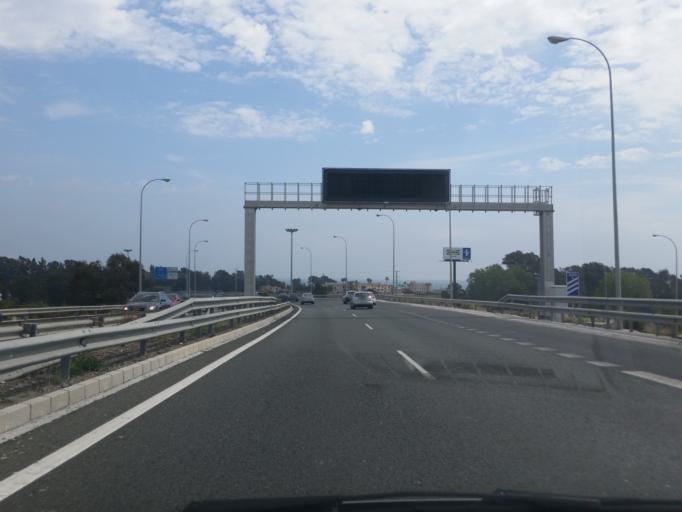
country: ES
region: Andalusia
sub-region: Provincia de Malaga
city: Torremolinos
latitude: 36.6490
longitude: -4.4857
